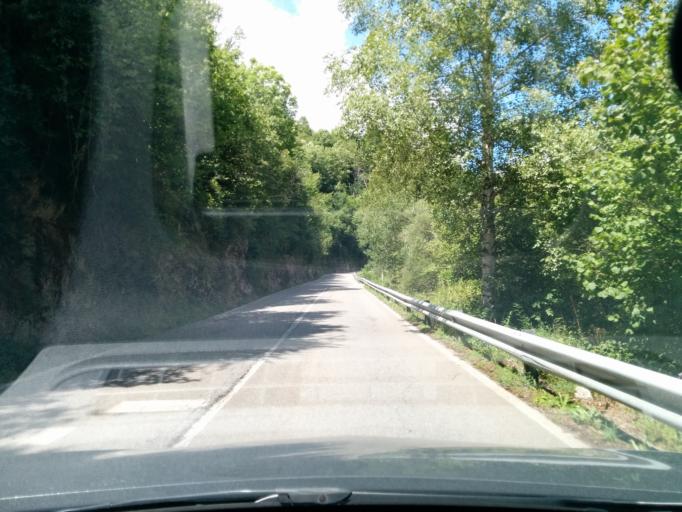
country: ES
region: Aragon
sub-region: Provincia de Huesca
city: Bielsa
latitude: 42.6372
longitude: 0.2153
